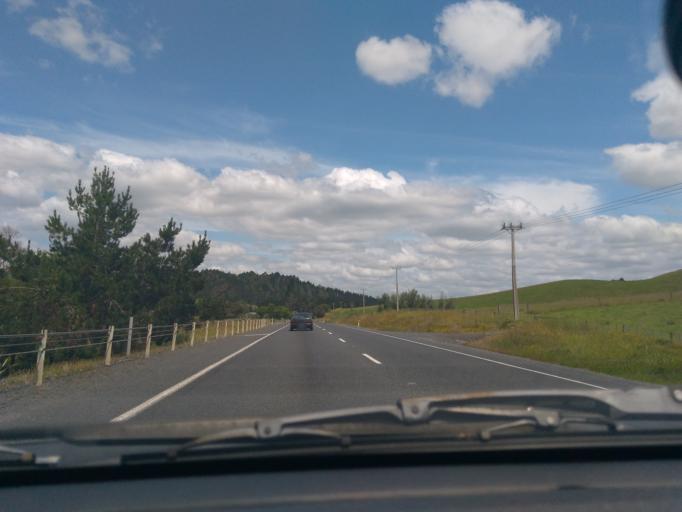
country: NZ
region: Northland
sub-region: Far North District
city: Kerikeri
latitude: -35.2778
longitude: 173.9524
